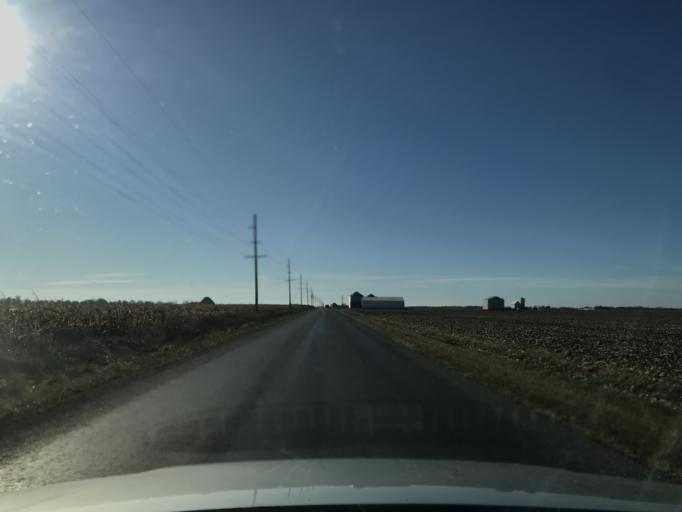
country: US
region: Illinois
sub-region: Hancock County
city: Carthage
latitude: 40.4807
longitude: -91.1781
